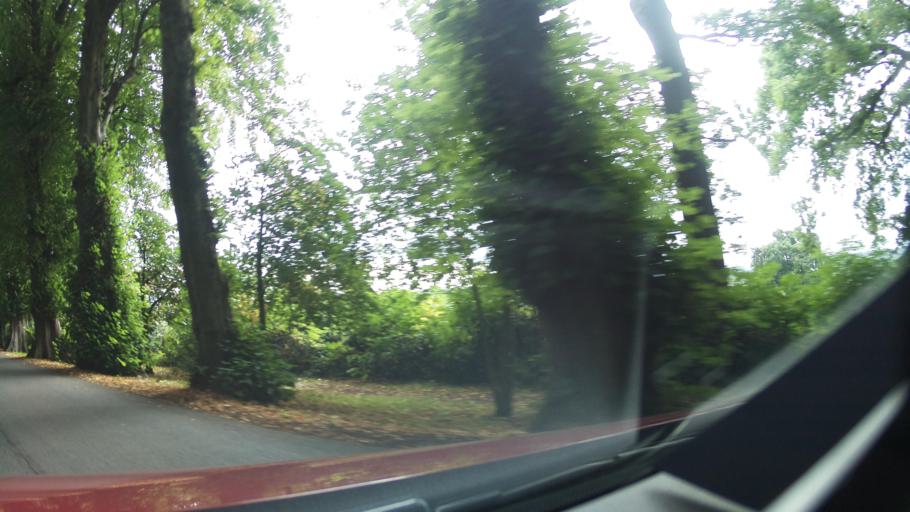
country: GB
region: England
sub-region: Staffordshire
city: Barlaston
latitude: 52.9476
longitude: -2.1576
